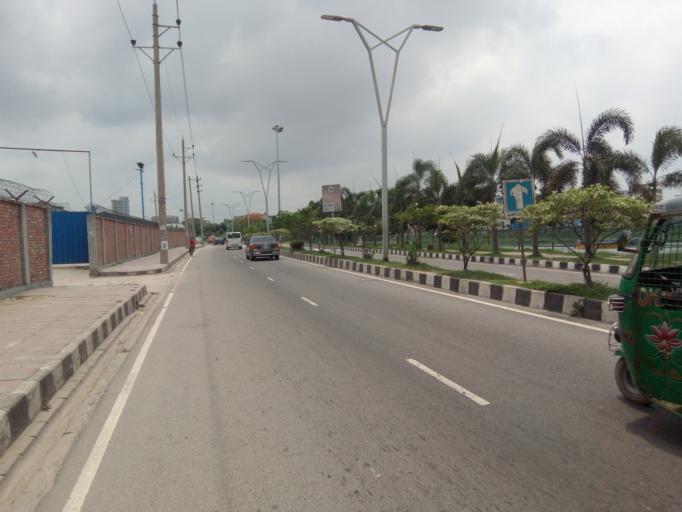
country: BD
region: Dhaka
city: Paltan
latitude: 23.7584
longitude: 90.4083
